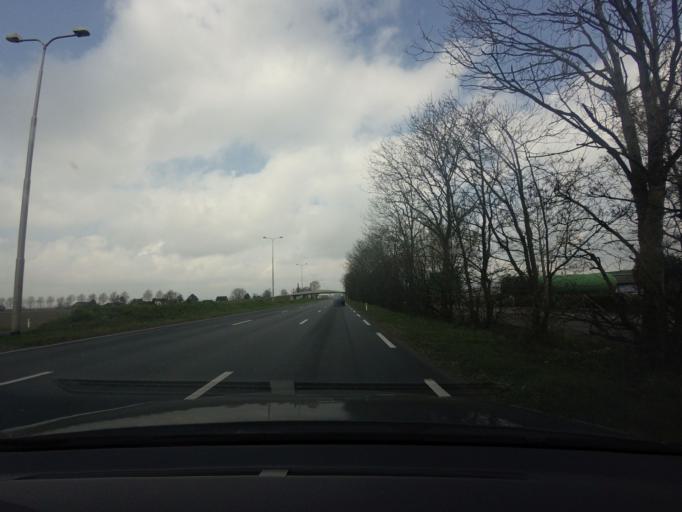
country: NL
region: North Holland
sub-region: Gemeente Aalsmeer
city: Aalsmeer
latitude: 52.2797
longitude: 4.7406
